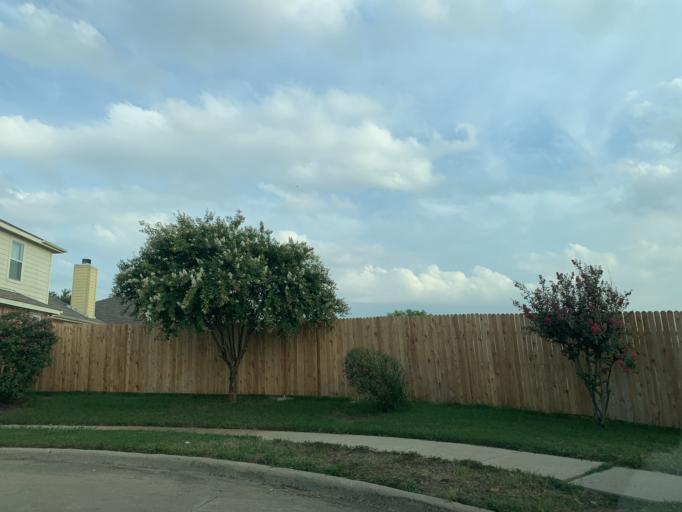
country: US
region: Texas
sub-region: Tarrant County
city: Keller
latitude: 32.9411
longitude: -97.2624
